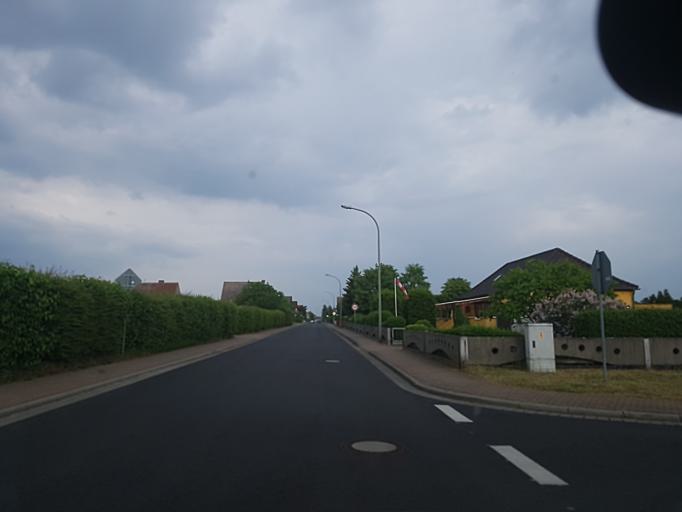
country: DE
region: Saxony-Anhalt
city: Elster
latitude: 51.8319
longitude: 12.8164
